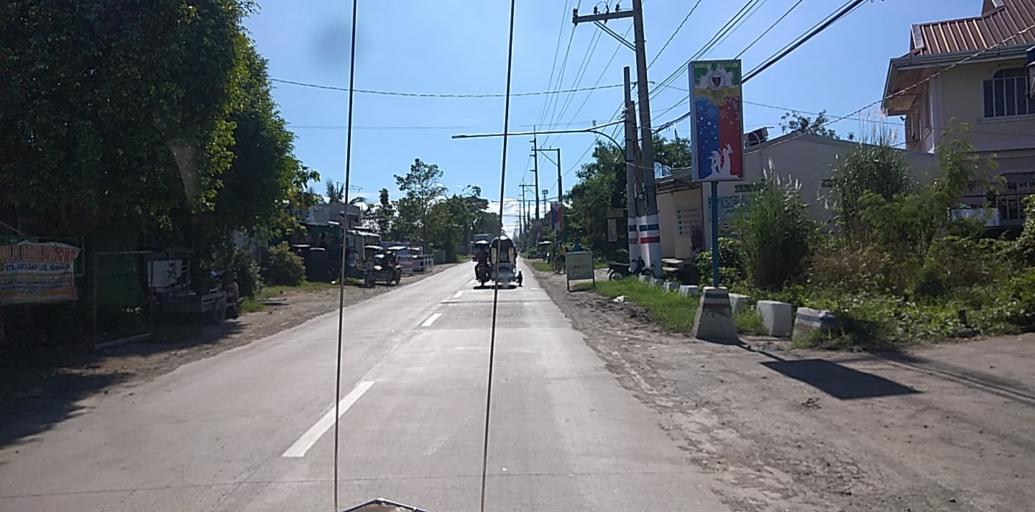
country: PH
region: Central Luzon
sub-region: Province of Pampanga
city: San Luis
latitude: 15.0506
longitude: 120.7829
